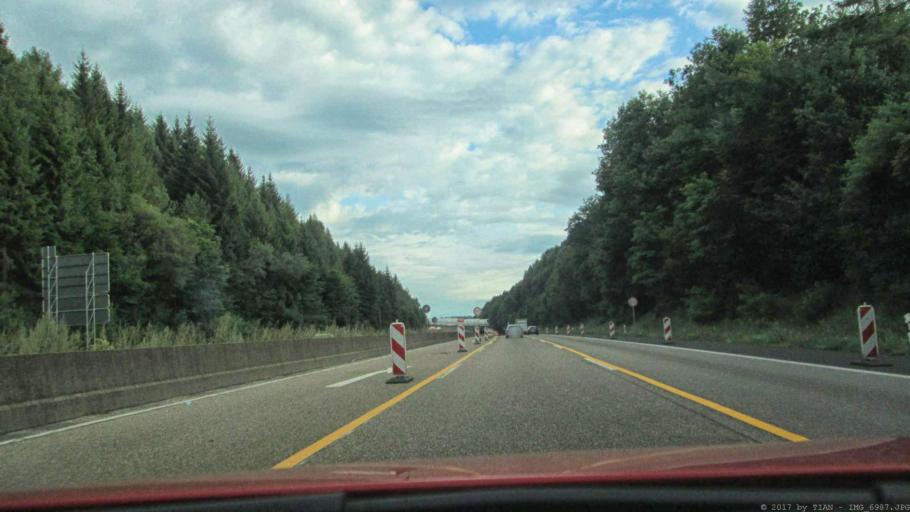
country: DE
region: Bavaria
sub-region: Regierungsbezirk Unterfranken
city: Motten
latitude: 50.3694
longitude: 9.7322
